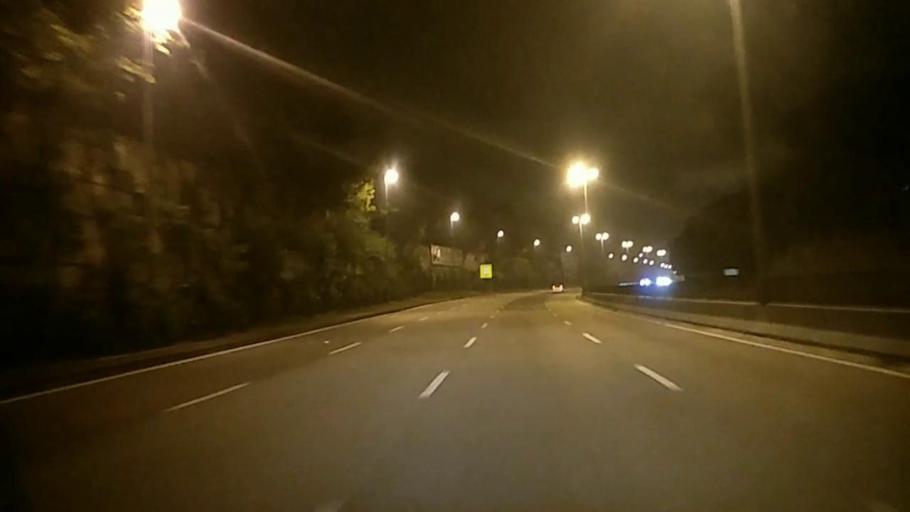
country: MY
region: Kuala Lumpur
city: Kuala Lumpur
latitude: 3.1897
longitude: 101.6197
